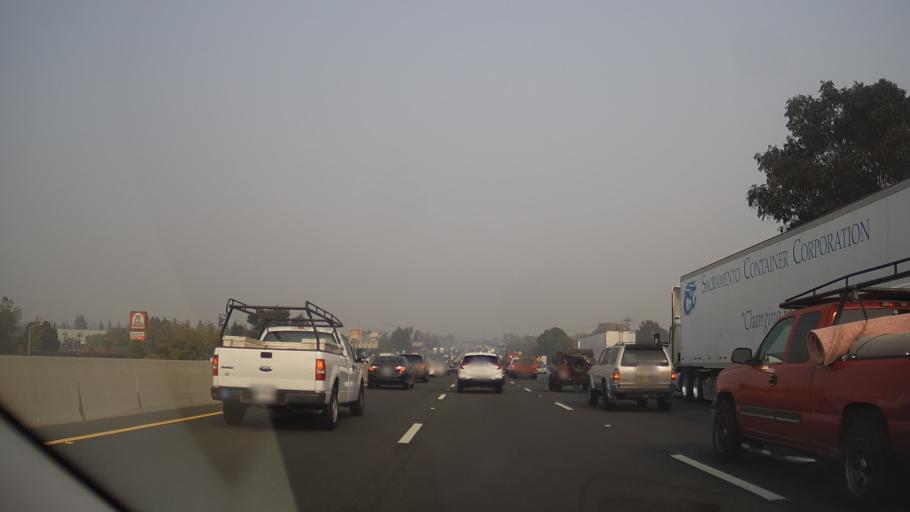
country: US
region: California
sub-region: Solano County
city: Fairfield
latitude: 38.2521
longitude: -122.0673
